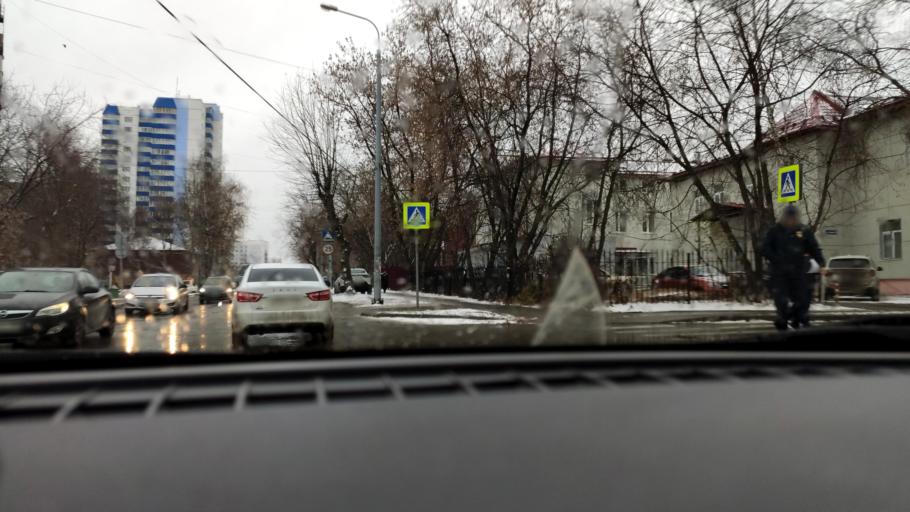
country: RU
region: Perm
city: Perm
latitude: 58.0277
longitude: 56.3075
